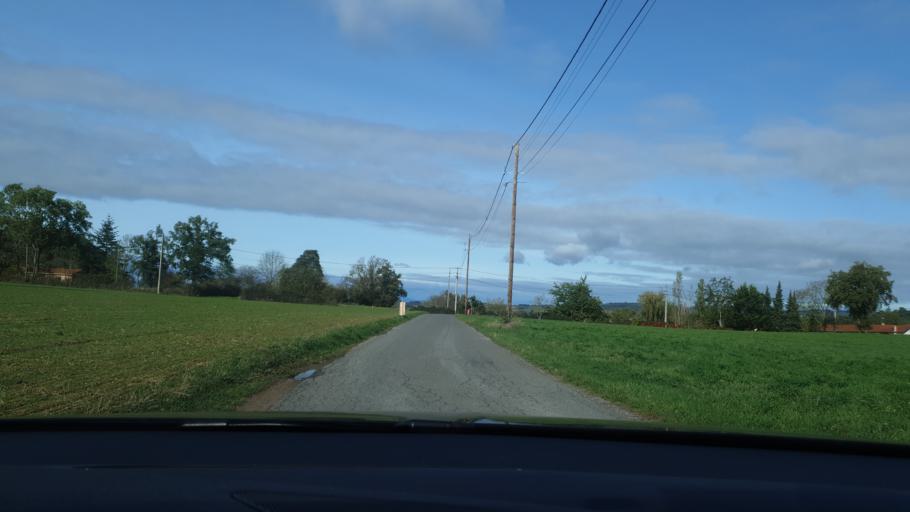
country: FR
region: Rhone-Alpes
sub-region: Departement du Rhone
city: Haute-Rivoire
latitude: 45.7276
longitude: 4.3796
